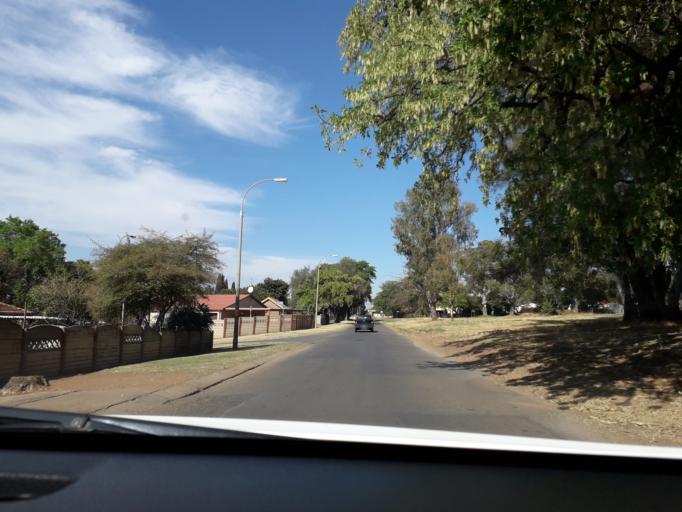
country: ZA
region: Gauteng
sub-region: City of Johannesburg Metropolitan Municipality
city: Modderfontein
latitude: -26.0845
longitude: 28.1965
